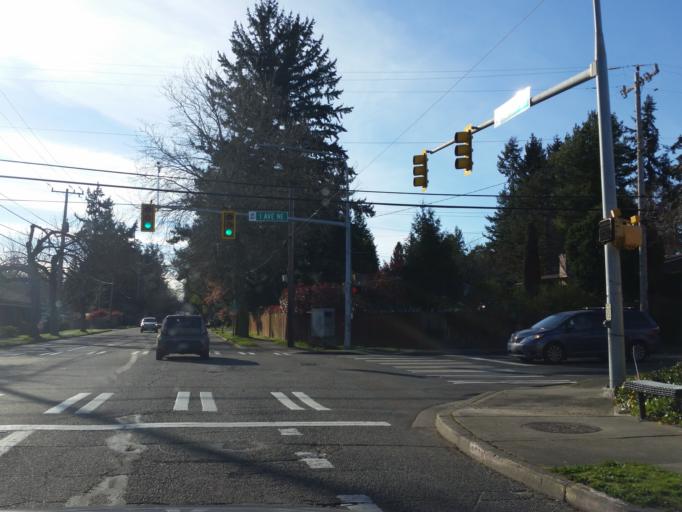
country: US
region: Washington
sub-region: King County
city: Shoreline
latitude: 47.7633
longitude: -122.3294
